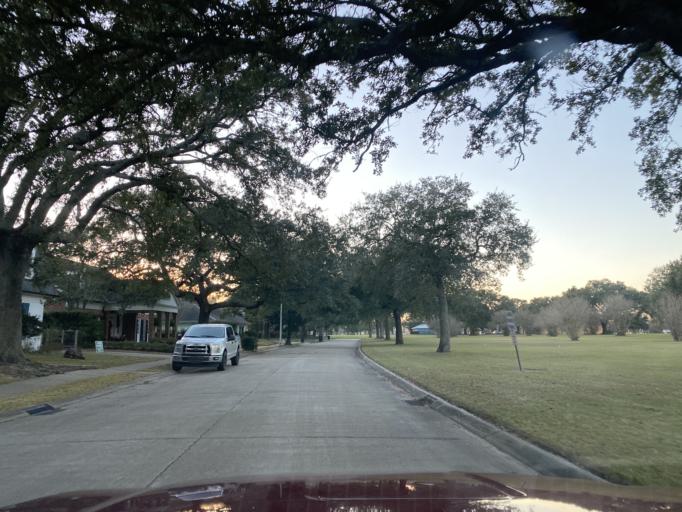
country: US
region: Louisiana
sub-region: Orleans Parish
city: New Orleans
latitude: 30.0293
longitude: -90.0584
